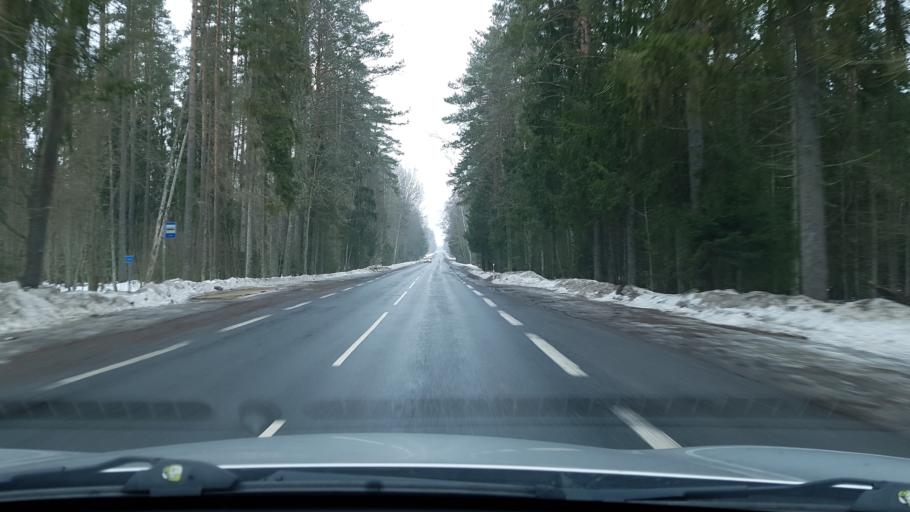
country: EE
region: Valgamaa
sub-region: Torva linn
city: Torva
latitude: 58.1717
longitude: 25.9633
